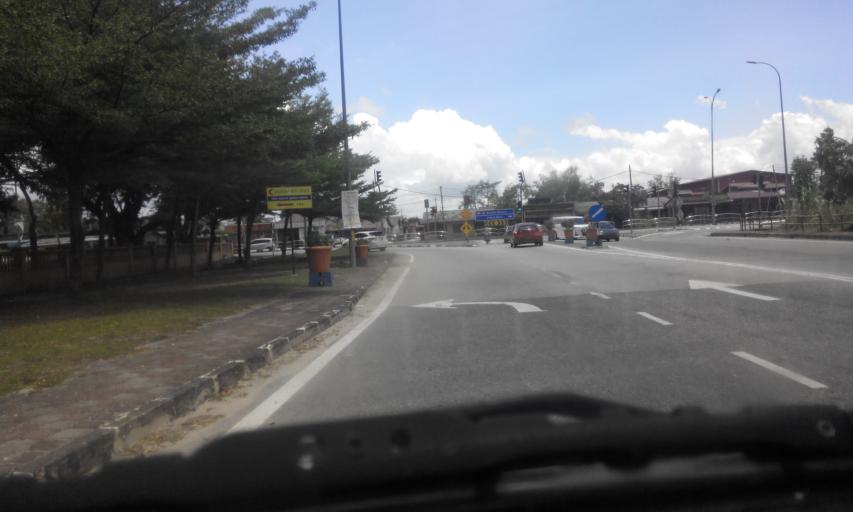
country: MY
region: Perak
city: Parit Buntar
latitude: 5.1266
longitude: 100.4912
